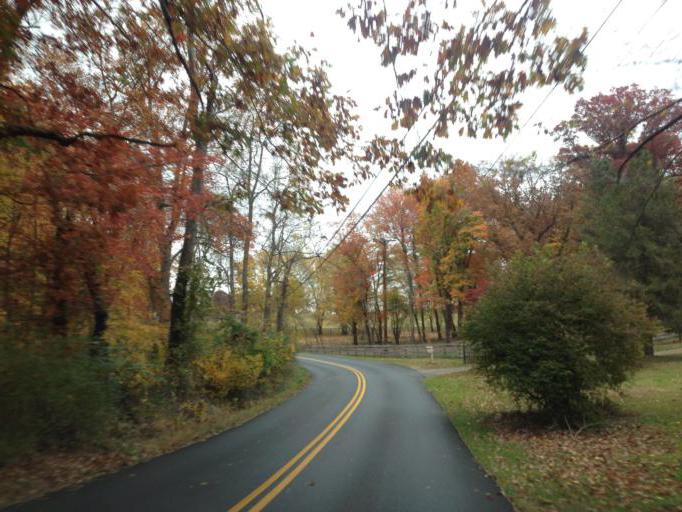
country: US
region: Maryland
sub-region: Baltimore County
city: Randallstown
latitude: 39.3583
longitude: -76.8546
